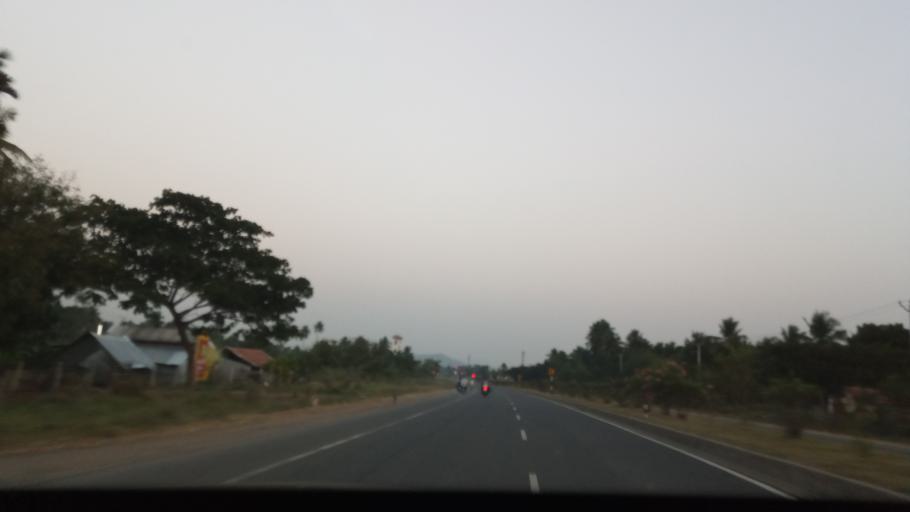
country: IN
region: Tamil Nadu
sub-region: Salem
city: Belur
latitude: 11.6549
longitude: 78.3405
